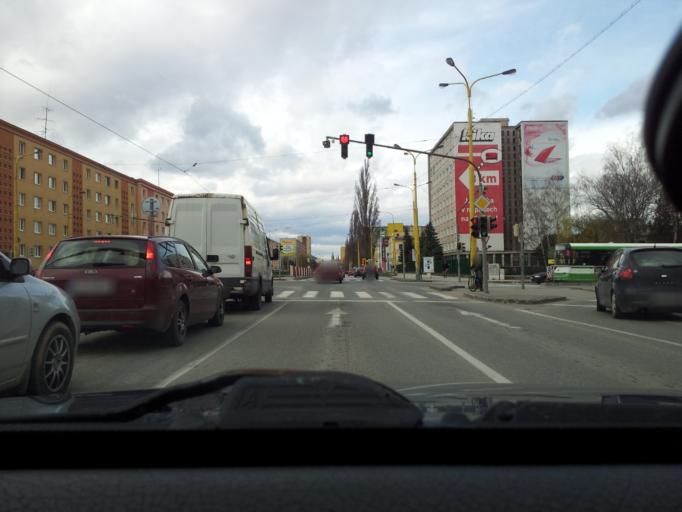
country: SK
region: Kosicky
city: Kosice
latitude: 48.7041
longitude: 21.2624
